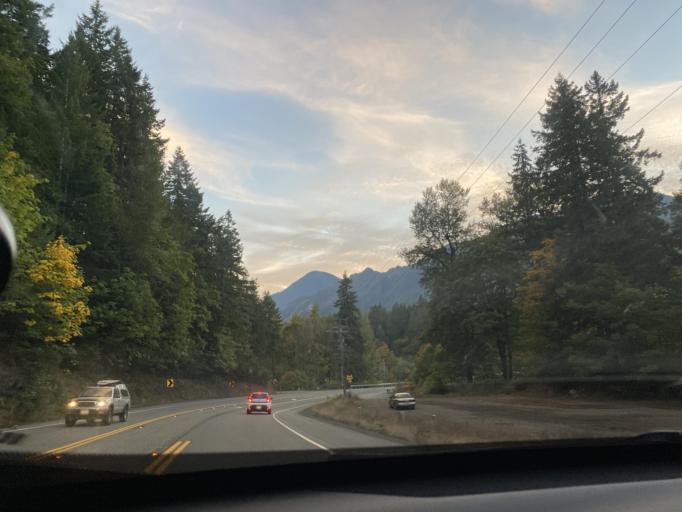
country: US
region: Washington
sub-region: Clallam County
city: Port Angeles
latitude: 48.0664
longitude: -123.5758
